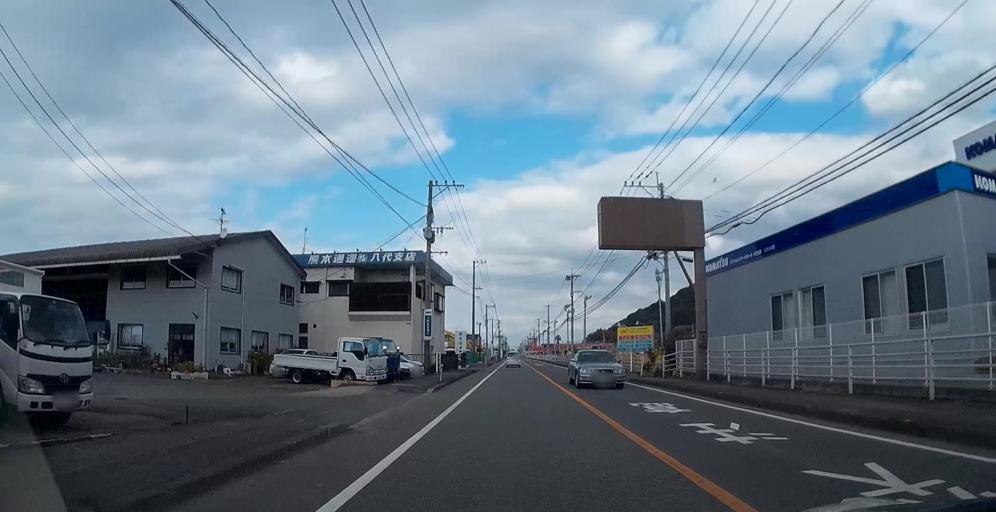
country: JP
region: Kumamoto
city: Yatsushiro
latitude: 32.4669
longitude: 130.6048
